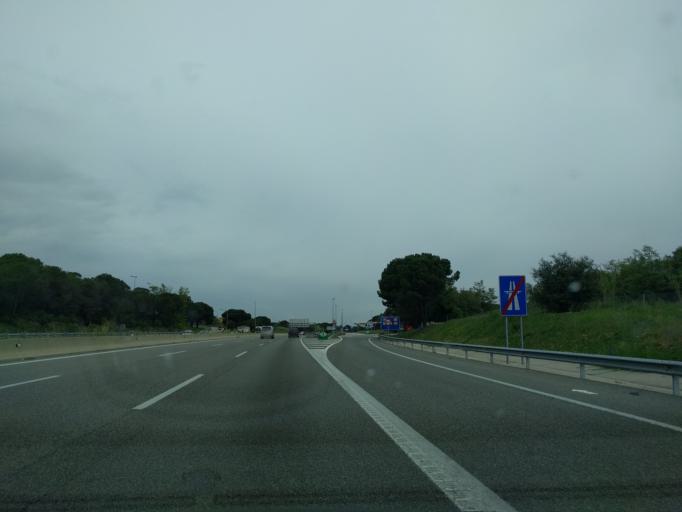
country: ES
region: Catalonia
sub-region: Provincia de Girona
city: Vilobi d'Onyar
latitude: 41.9041
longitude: 2.7734
